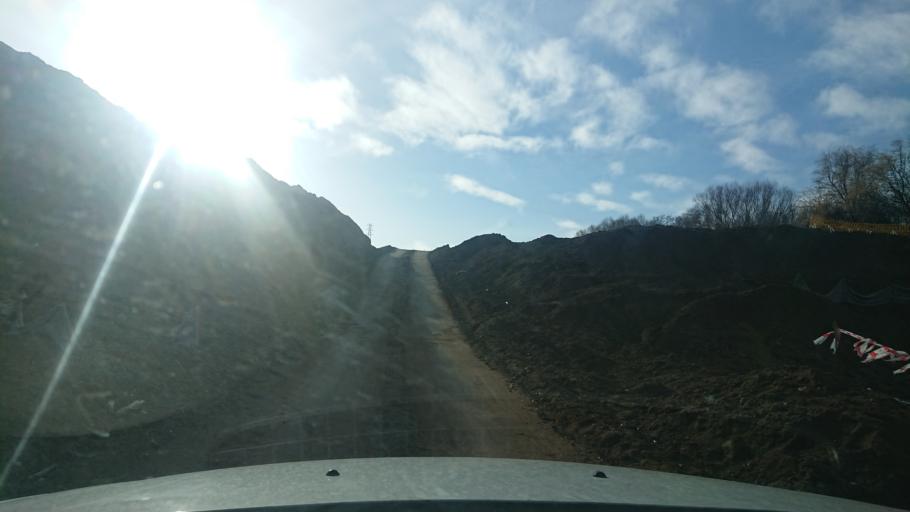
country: TR
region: Aksaray
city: Agacoren
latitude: 38.8611
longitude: 33.9416
